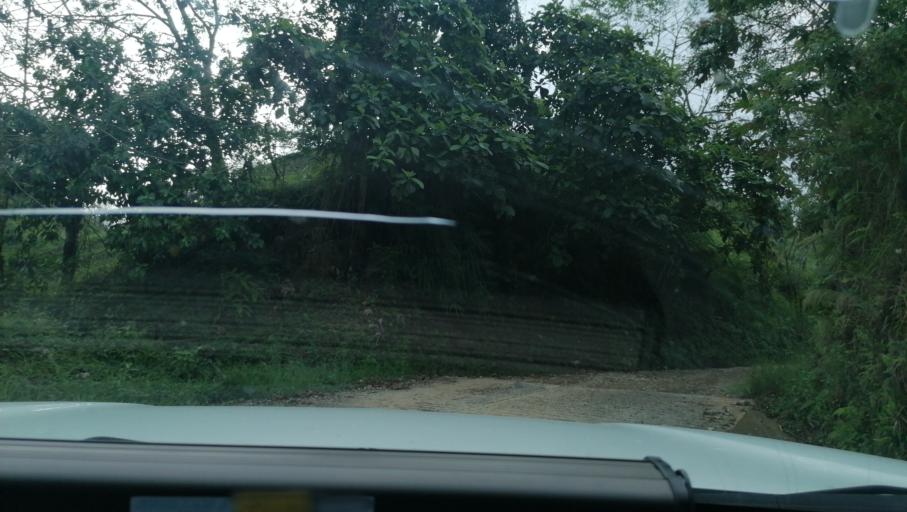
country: MX
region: Chiapas
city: Ixtacomitan
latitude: 17.3358
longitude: -93.1108
